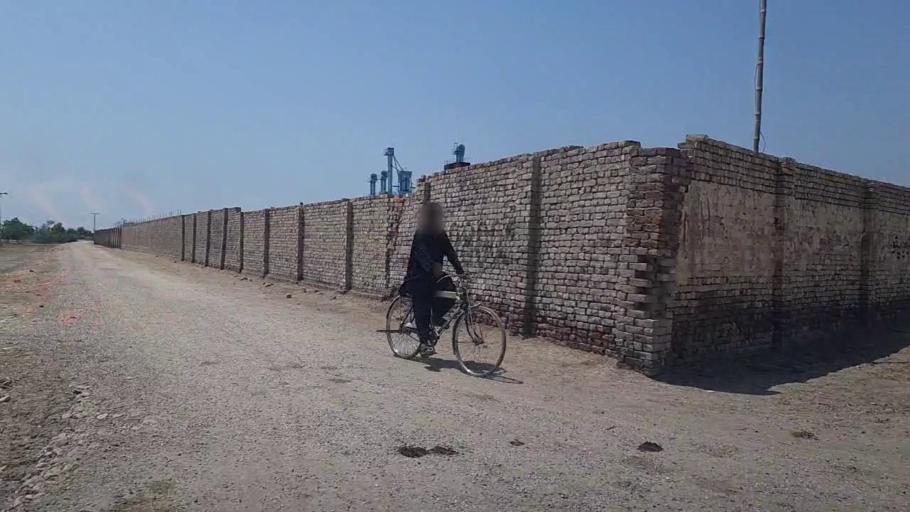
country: PK
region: Sindh
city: Ubauro
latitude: 28.1721
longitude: 69.7627
